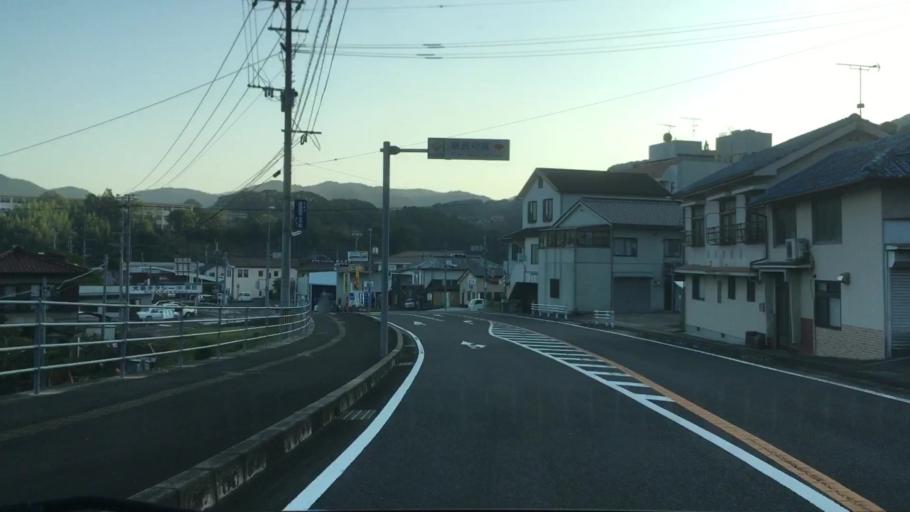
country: JP
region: Nagasaki
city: Sasebo
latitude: 33.0031
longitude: 129.7303
